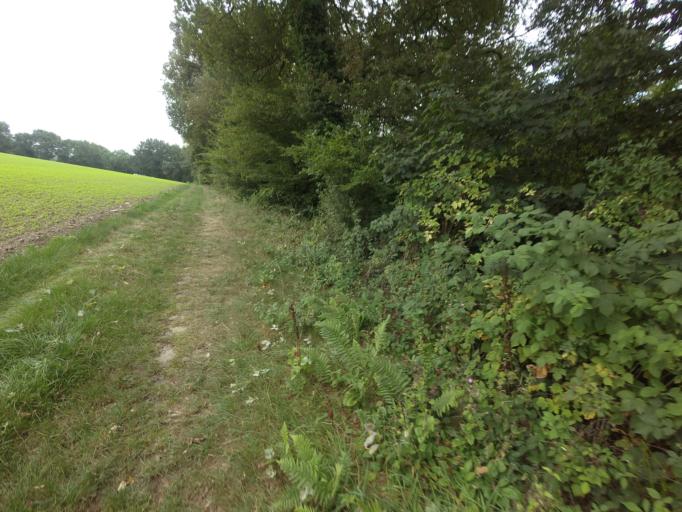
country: NL
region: Limburg
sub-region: Gemeente Simpelveld
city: Simpelveld
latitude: 50.7990
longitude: 5.9881
